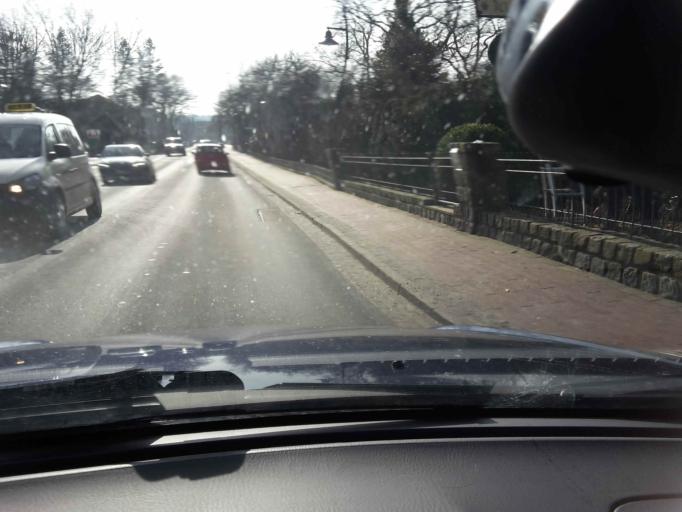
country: DE
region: Lower Saxony
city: Jesteburg
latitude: 53.3055
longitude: 9.9531
